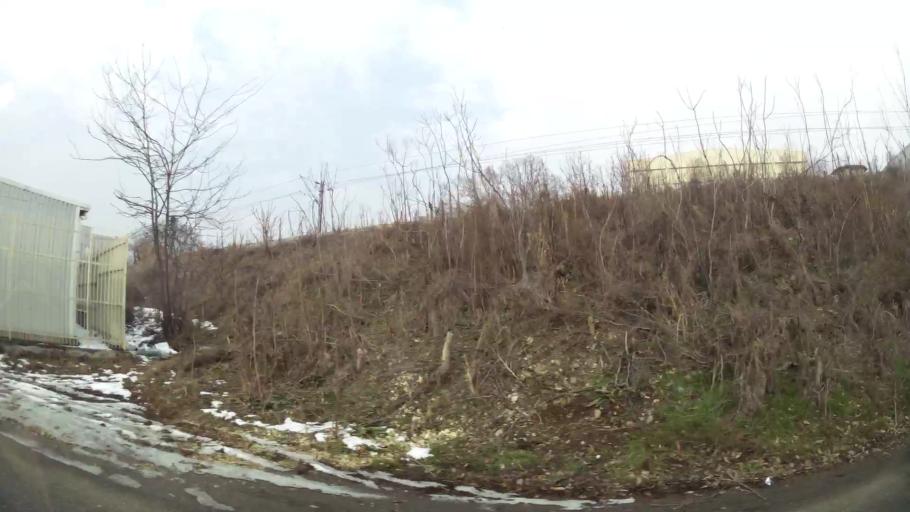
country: MK
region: Cair
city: Cair
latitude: 41.9971
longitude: 21.4663
